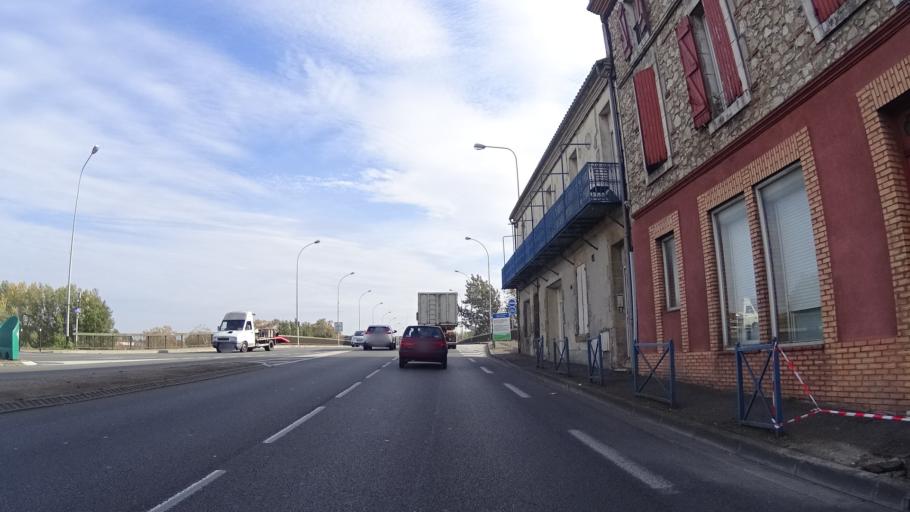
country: FR
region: Aquitaine
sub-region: Departement du Lot-et-Garonne
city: Le Passage
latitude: 44.1947
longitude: 0.6080
